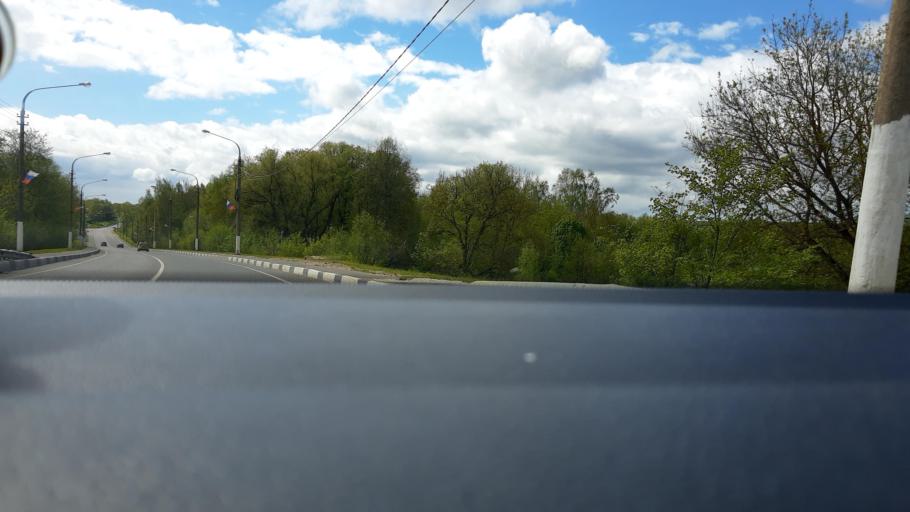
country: RU
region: Moskovskaya
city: Yakhroma
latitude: 56.3252
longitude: 37.4977
